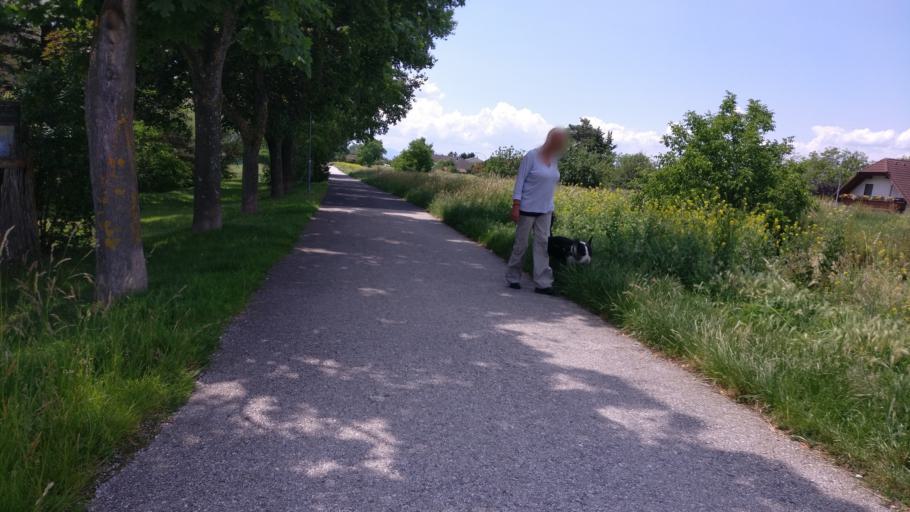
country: AT
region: Lower Austria
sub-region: Politischer Bezirk Wiener Neustadt
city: Lichtenworth
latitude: 47.8350
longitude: 16.2658
